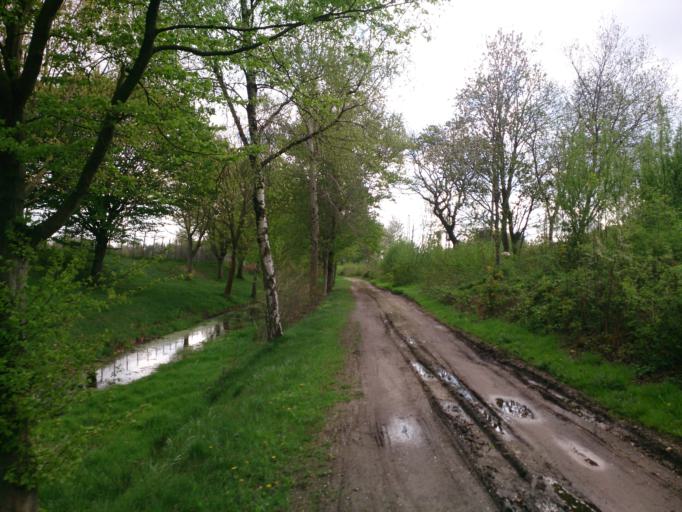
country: DE
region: Hamburg
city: Harburg
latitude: 53.4722
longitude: 9.9105
